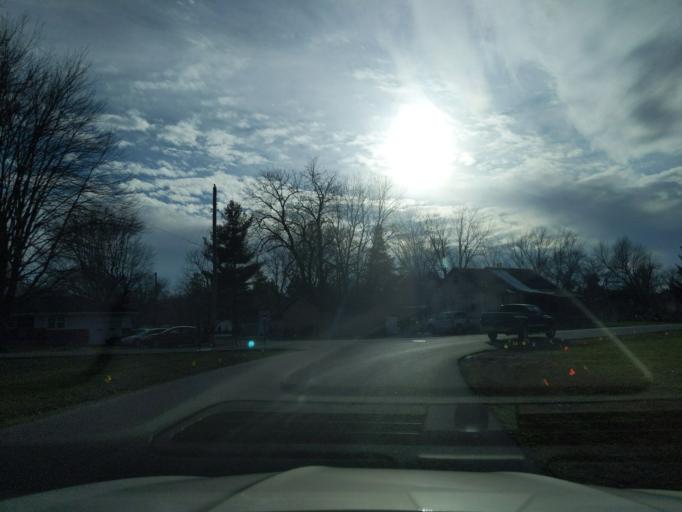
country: US
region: Indiana
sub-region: Decatur County
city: Westport
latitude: 39.1798
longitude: -85.5665
